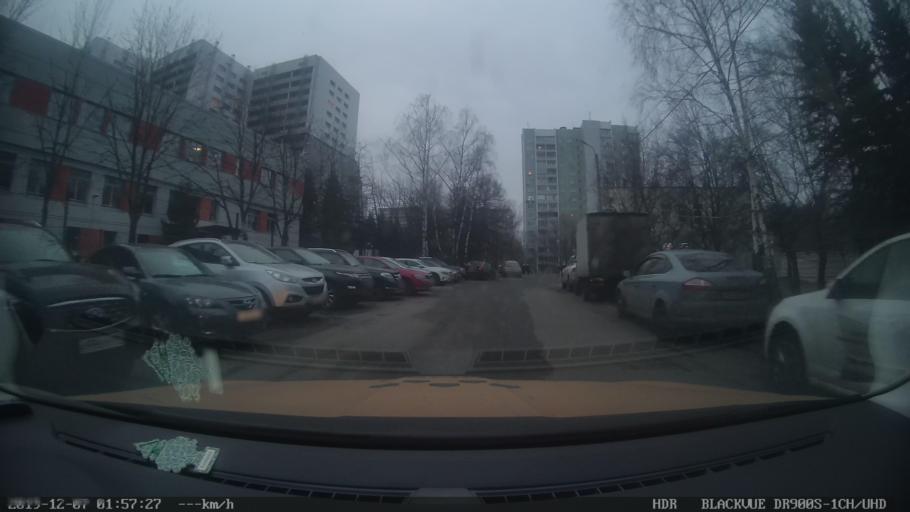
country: RU
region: Moscow
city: Troparevo
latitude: 55.6651
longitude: 37.4948
